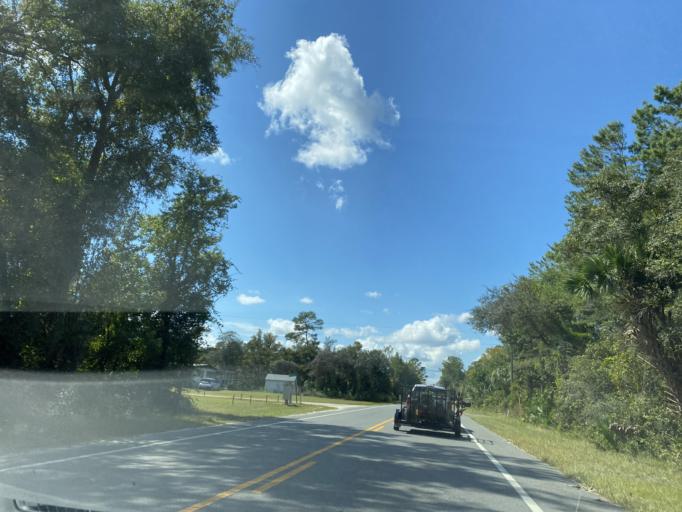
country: US
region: Florida
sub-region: Lake County
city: Lake Mack-Forest Hills
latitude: 29.0171
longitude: -81.4895
